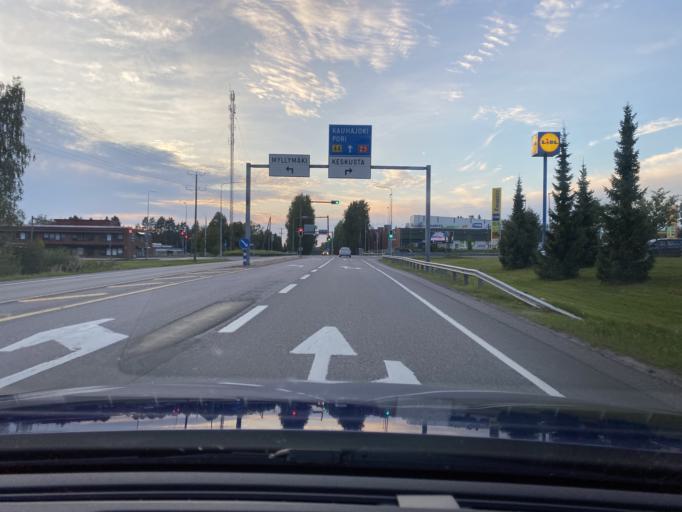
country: FI
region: Satakunta
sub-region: Pohjois-Satakunta
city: Kankaanpaeae
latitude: 61.8120
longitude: 22.3758
